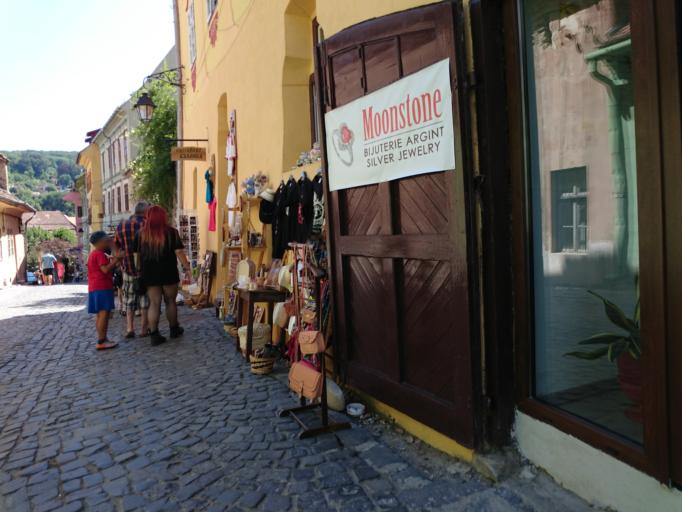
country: RO
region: Mures
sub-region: Municipiul Sighisoara
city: Sighisoara
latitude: 46.2187
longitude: 24.7933
